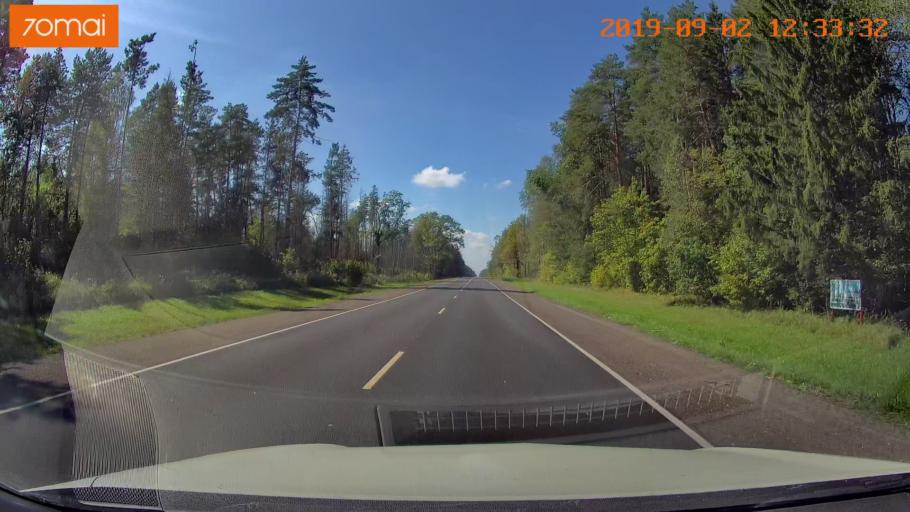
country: RU
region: Smolensk
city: Shumyachi
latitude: 53.8171
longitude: 32.4262
